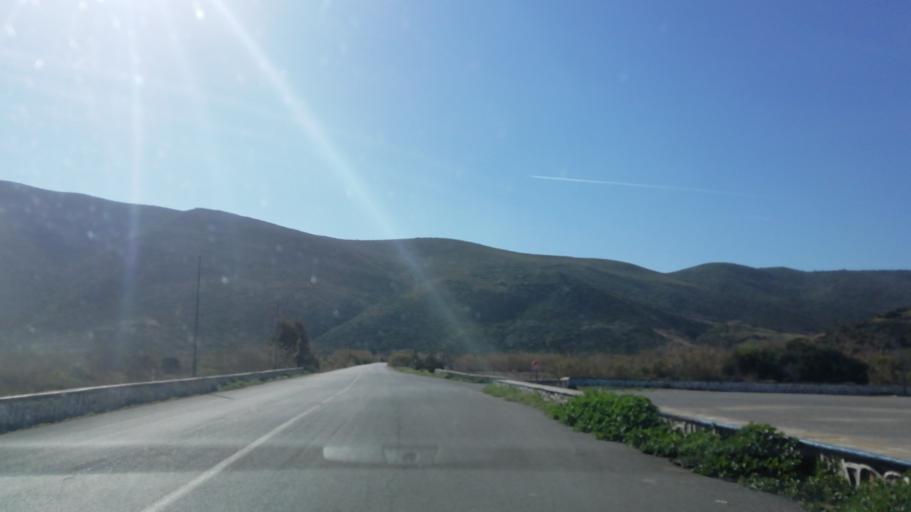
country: DZ
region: Ain Temouchent
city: El Amria
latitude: 35.6381
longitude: -1.0587
